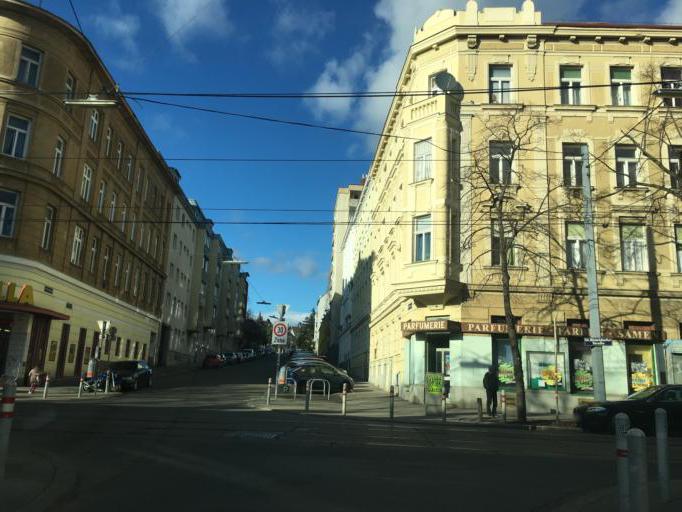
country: AT
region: Lower Austria
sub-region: Politischer Bezirk Modling
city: Perchtoldsdorf
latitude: 48.1970
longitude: 16.2843
